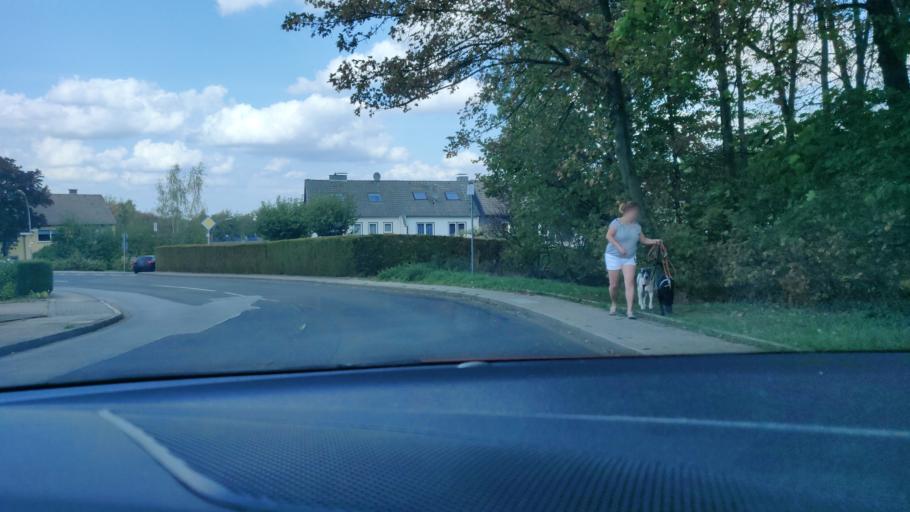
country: DE
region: North Rhine-Westphalia
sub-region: Regierungsbezirk Dusseldorf
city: Velbert
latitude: 51.3585
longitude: 7.0396
